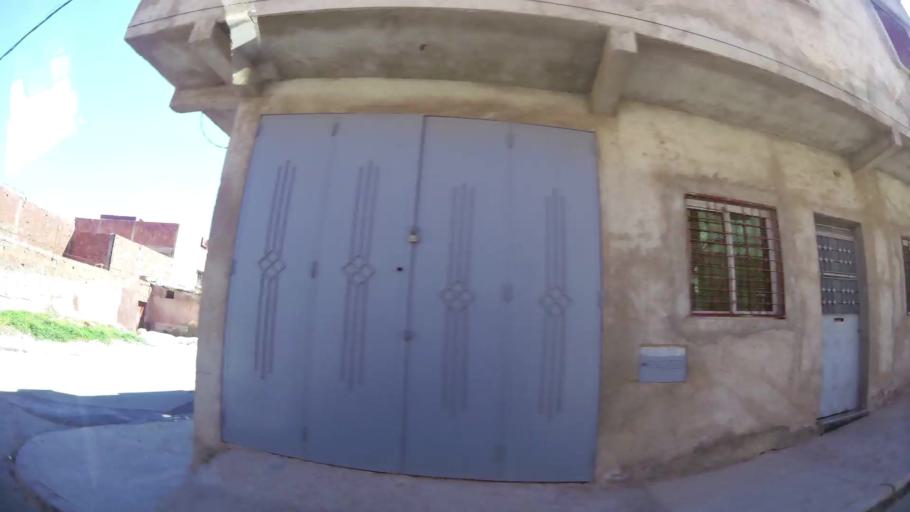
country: MA
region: Oriental
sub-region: Oujda-Angad
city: Oujda
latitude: 34.6487
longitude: -1.8748
